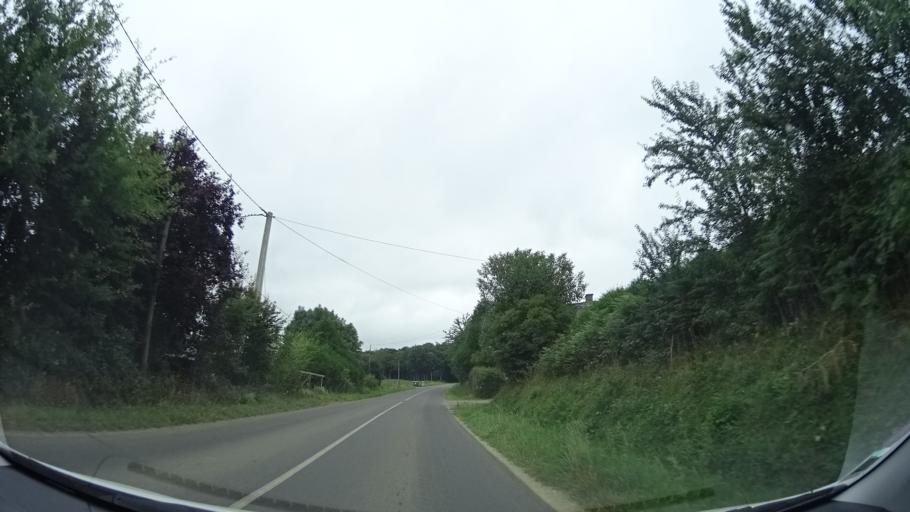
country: FR
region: Brittany
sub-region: Departement d'Ille-et-Vilaine
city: Pleugueneuc
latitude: 48.3498
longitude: -1.9266
